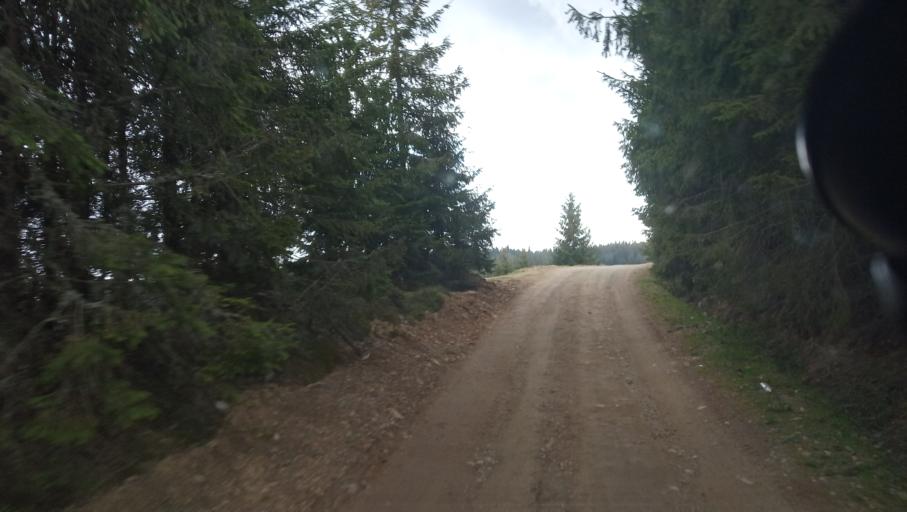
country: RO
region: Cluj
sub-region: Comuna Belis
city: Belis
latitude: 46.6310
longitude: 23.0444
